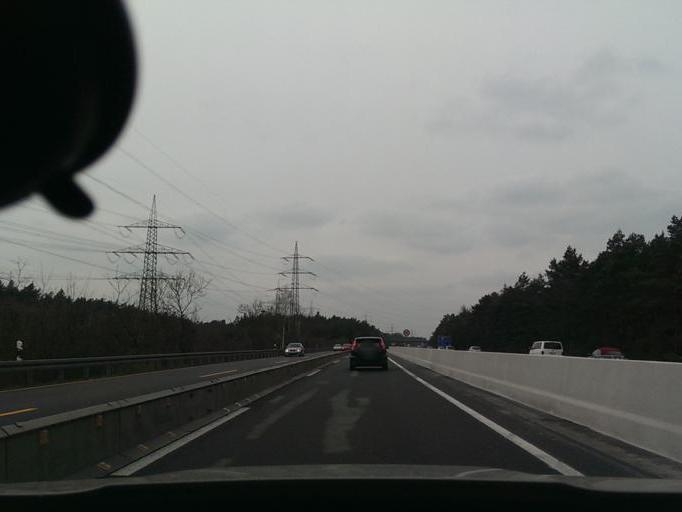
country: DE
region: North Rhine-Westphalia
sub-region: Regierungsbezirk Detmold
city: Hovelhof
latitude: 51.8444
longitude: 8.6772
